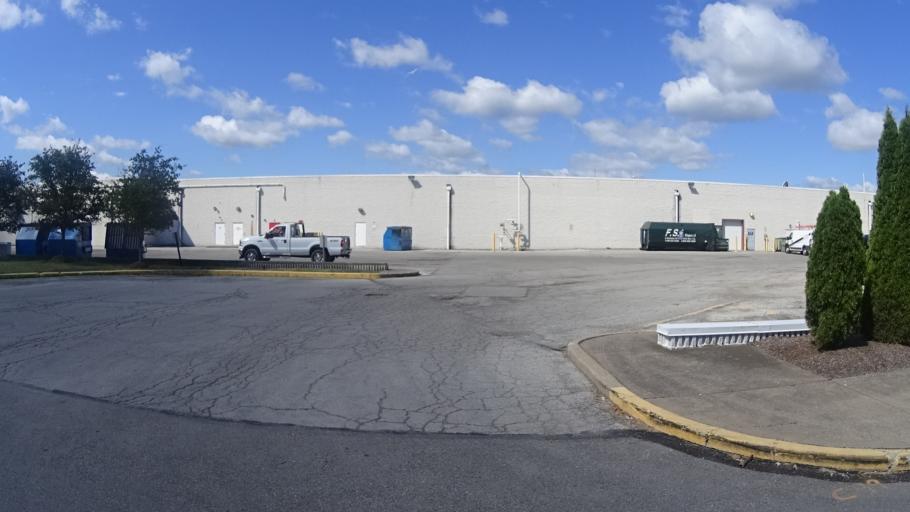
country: US
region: Ohio
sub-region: Erie County
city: Sandusky
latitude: 41.4195
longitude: -82.6688
